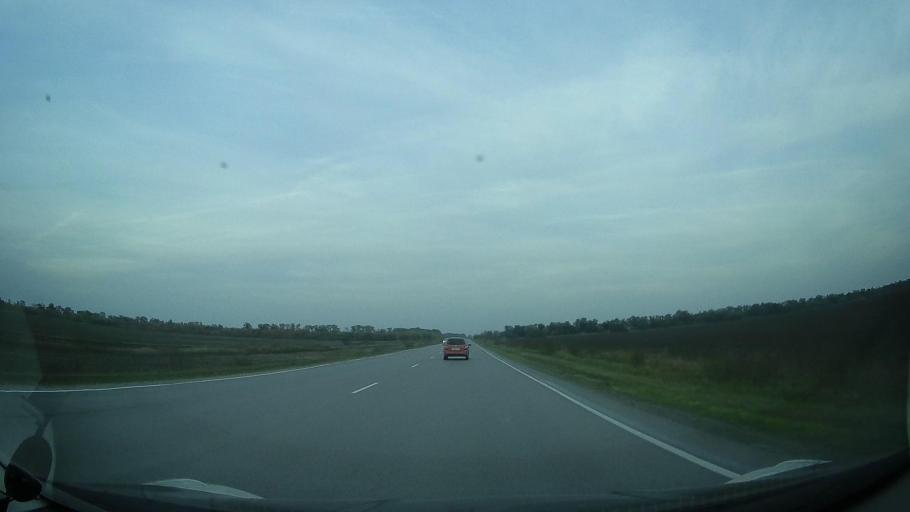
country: RU
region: Rostov
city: Ol'ginskaya
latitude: 47.1303
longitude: 39.9217
